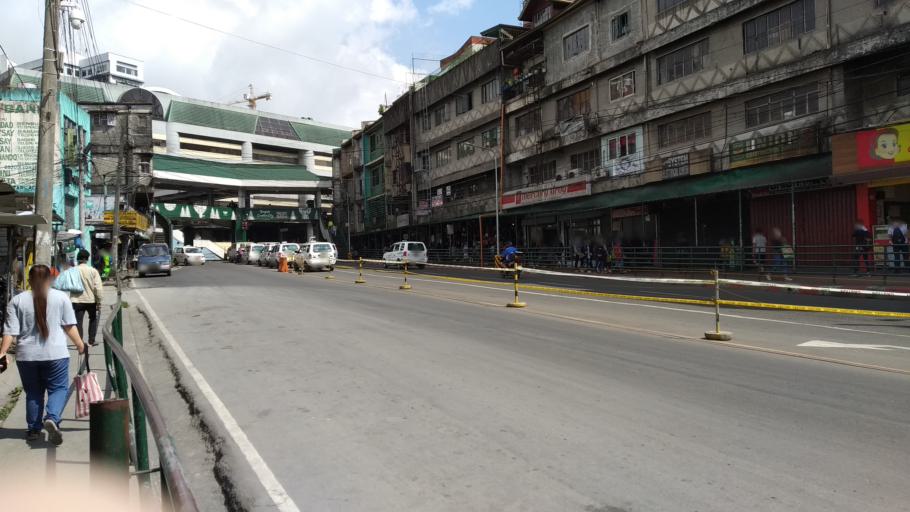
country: PH
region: Cordillera
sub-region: Baguio City
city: Baguio
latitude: 16.4174
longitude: 120.5954
